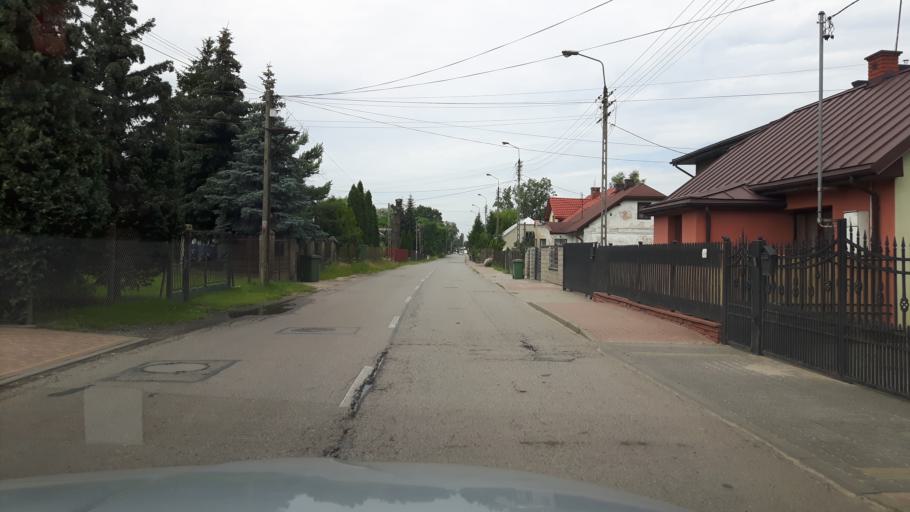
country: PL
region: Masovian Voivodeship
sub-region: Powiat wolominski
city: Kobylka
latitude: 52.3137
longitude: 21.2016
